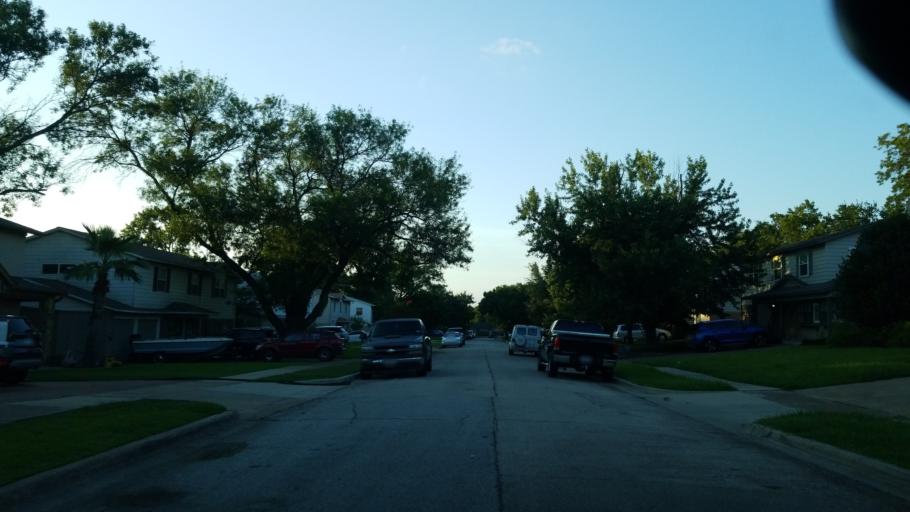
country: US
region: Texas
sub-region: Dallas County
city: Carrollton
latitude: 32.9443
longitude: -96.8824
